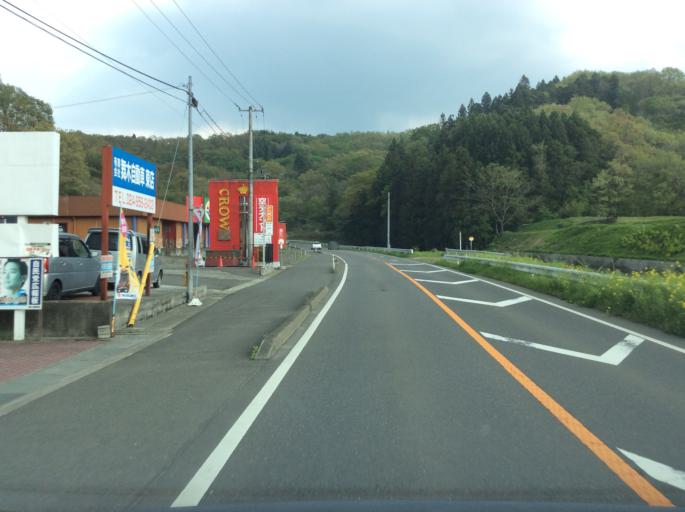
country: JP
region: Fukushima
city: Miharu
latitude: 37.4221
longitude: 140.4447
